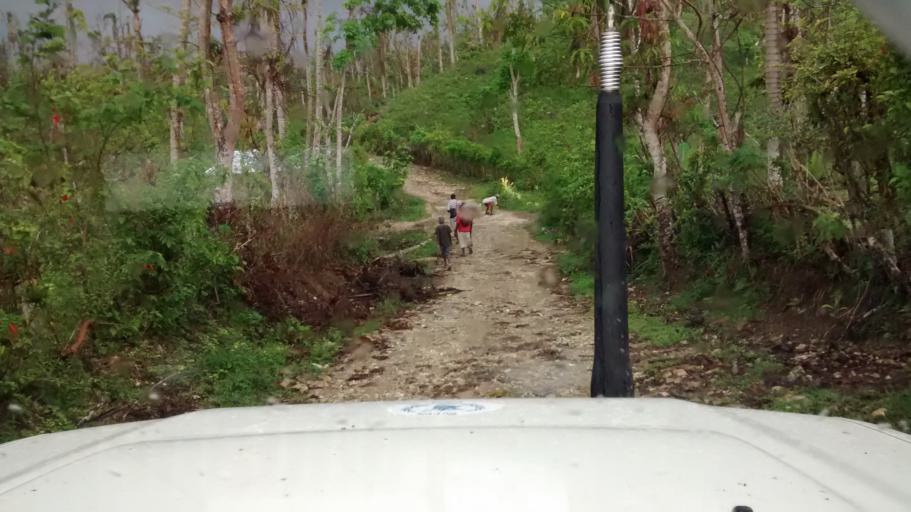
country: HT
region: Grandans
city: Moron
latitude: 18.5336
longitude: -74.1565
